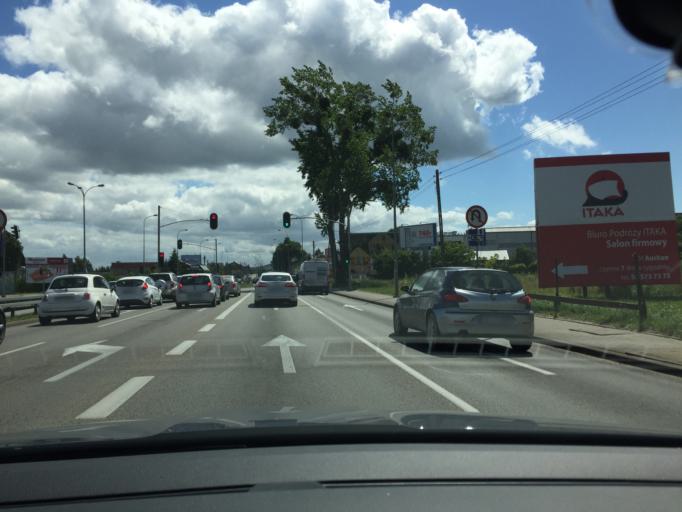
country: PL
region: Pomeranian Voivodeship
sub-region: Powiat wejherowski
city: Rumia
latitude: 54.5840
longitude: 18.3645
